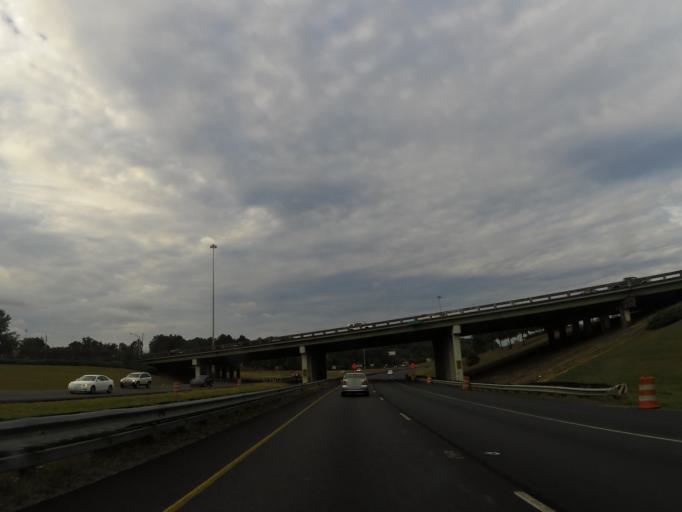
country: US
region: Alabama
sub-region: Shelby County
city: Alabaster
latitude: 33.2298
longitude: -86.8076
